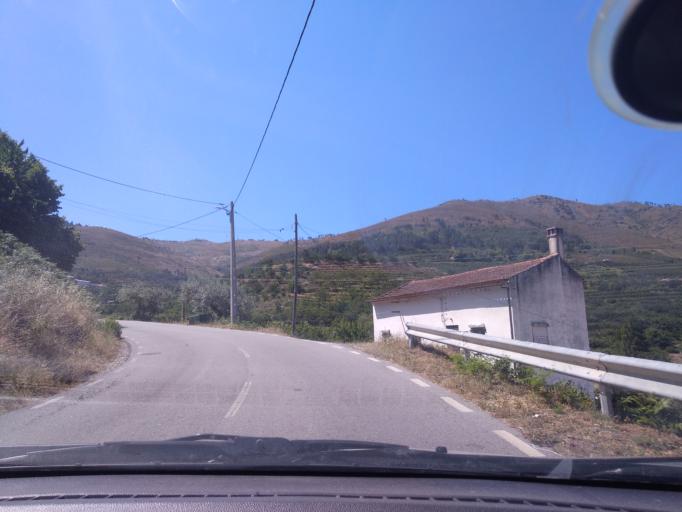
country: PT
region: Castelo Branco
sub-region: Concelho do Fundao
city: Fundao
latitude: 40.1226
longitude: -7.4894
